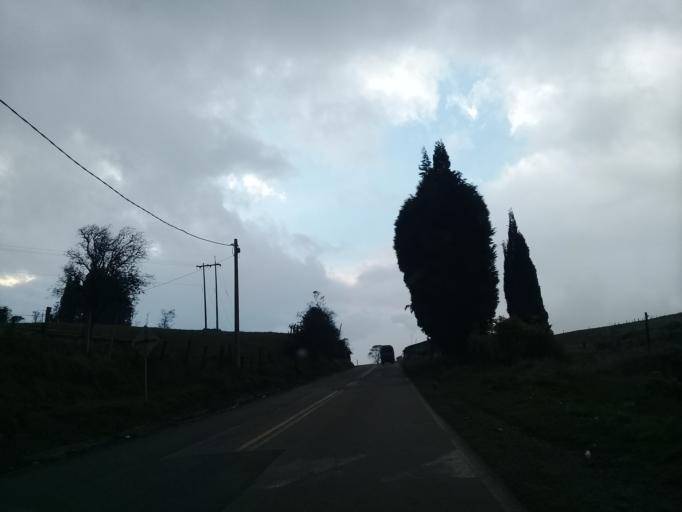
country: CO
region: Cundinamarca
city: Cogua
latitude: 5.0900
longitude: -74.0618
